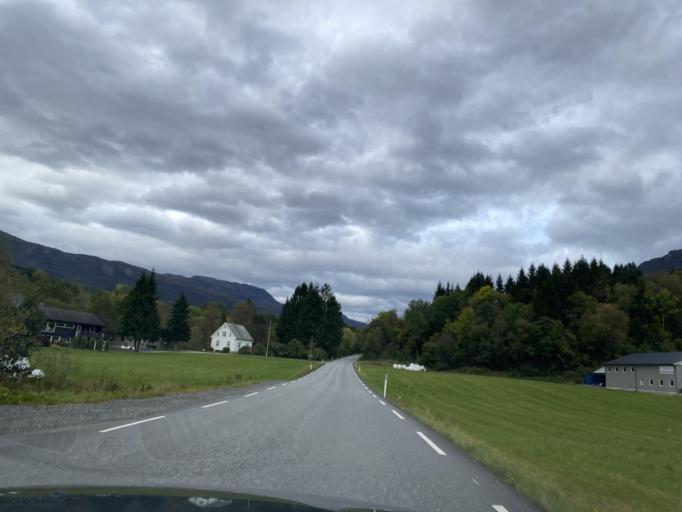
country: NO
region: Hordaland
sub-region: Etne
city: Etne
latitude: 59.6646
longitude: 5.9883
